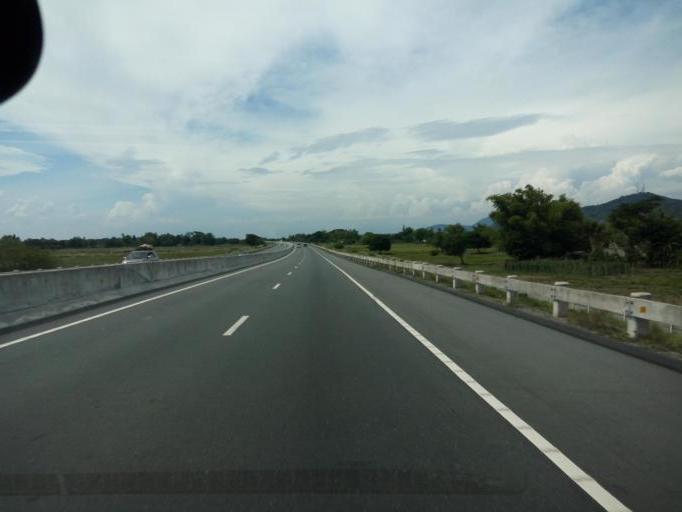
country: PH
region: Central Luzon
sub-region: Province of Nueva Ecija
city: Calancuasan Norte
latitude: 15.7787
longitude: 120.6415
